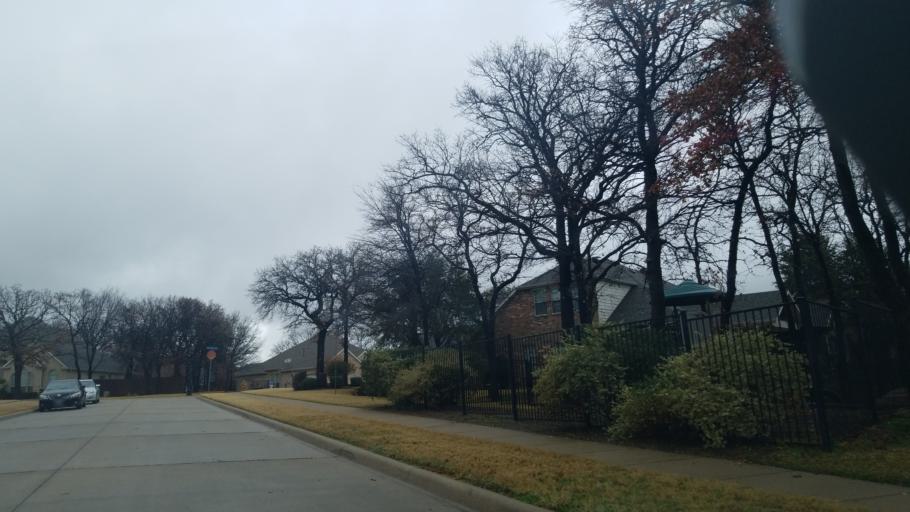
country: US
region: Texas
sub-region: Denton County
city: Corinth
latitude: 33.1442
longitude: -97.0873
